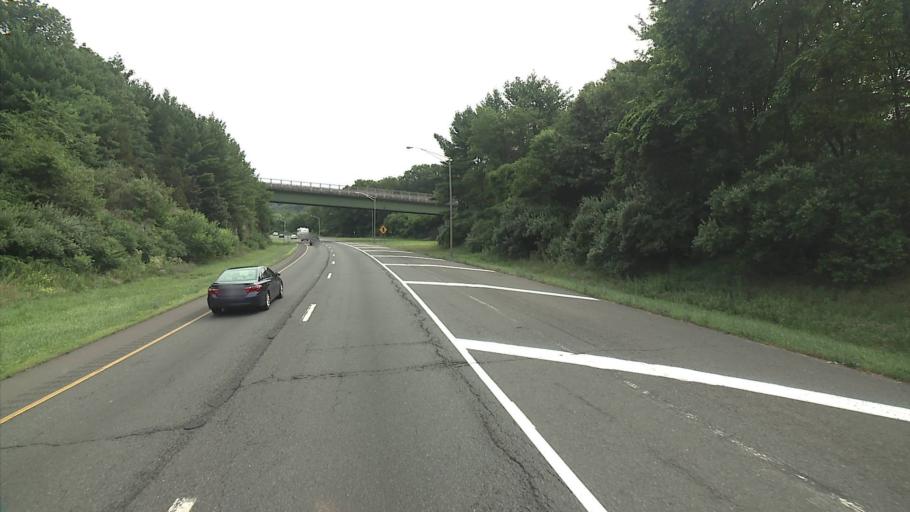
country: US
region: Connecticut
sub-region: Fairfield County
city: Newtown
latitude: 41.4144
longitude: -73.2665
